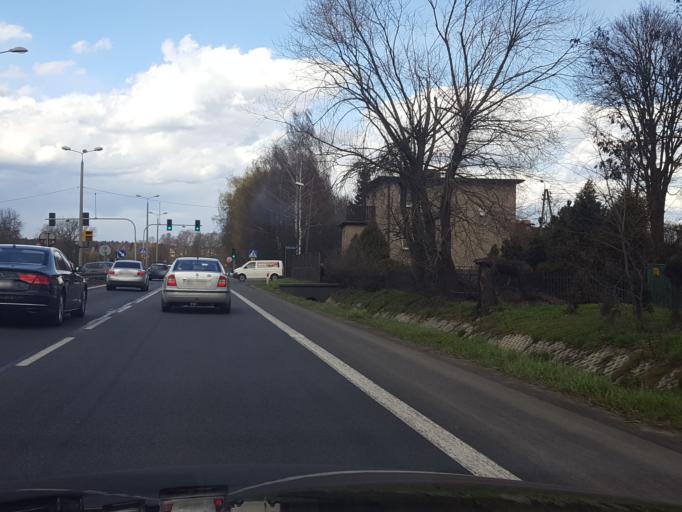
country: PL
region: Silesian Voivodeship
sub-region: Powiat pszczynski
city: Piasek
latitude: 50.0028
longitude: 18.9511
